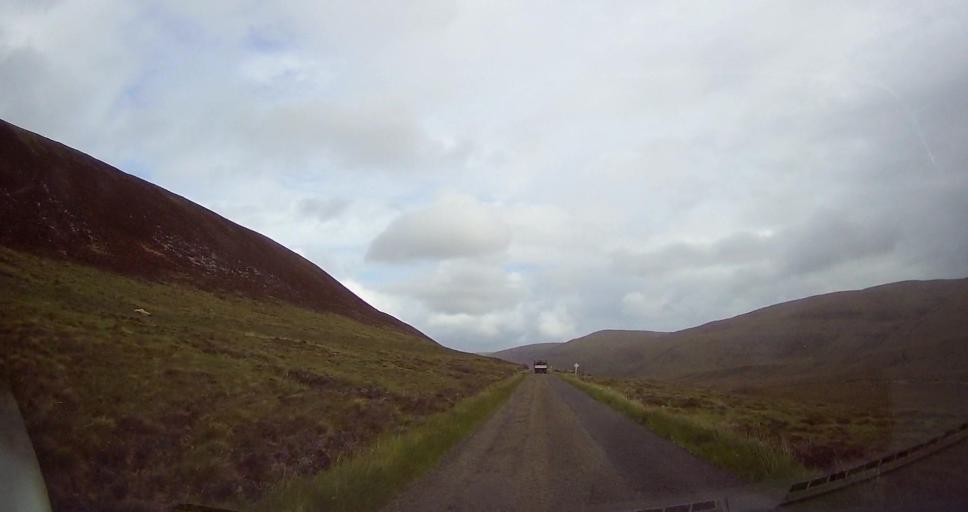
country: GB
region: Scotland
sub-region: Orkney Islands
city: Stromness
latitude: 58.8814
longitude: -3.3678
